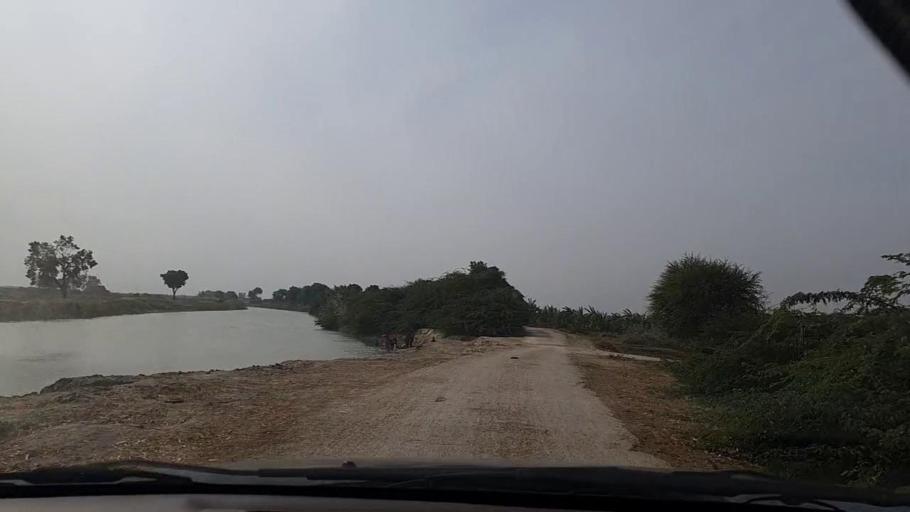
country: PK
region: Sindh
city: Thatta
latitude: 24.5771
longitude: 67.8819
